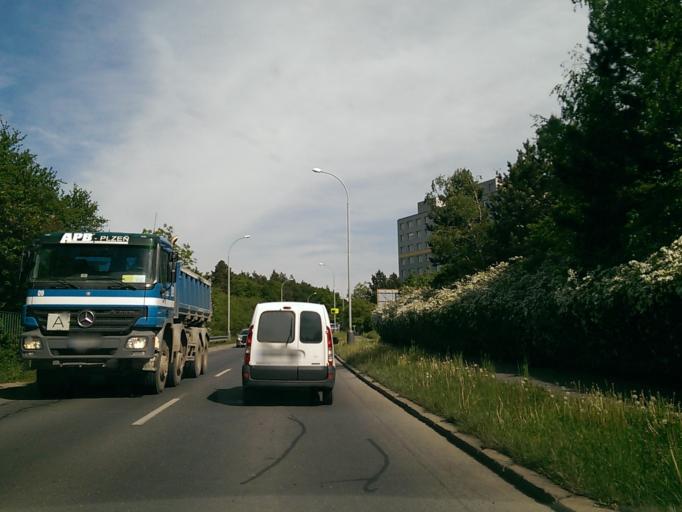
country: CZ
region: Central Bohemia
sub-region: Okres Praha-Zapad
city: Pruhonice
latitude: 50.0393
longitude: 14.5162
